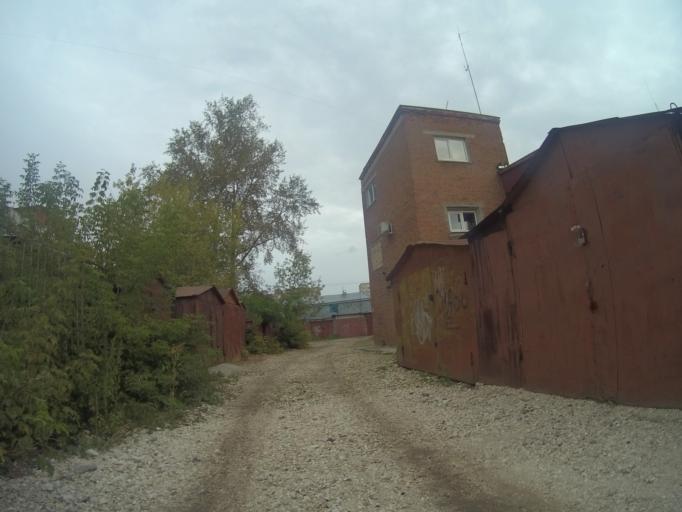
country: RU
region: Vladimir
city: Vladimir
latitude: 56.1150
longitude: 40.3490
